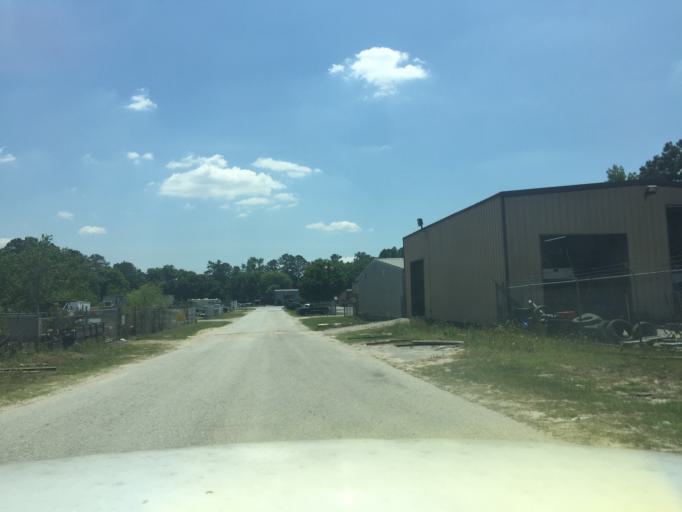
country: US
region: Georgia
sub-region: Chatham County
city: Garden City
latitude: 32.0482
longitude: -81.1742
